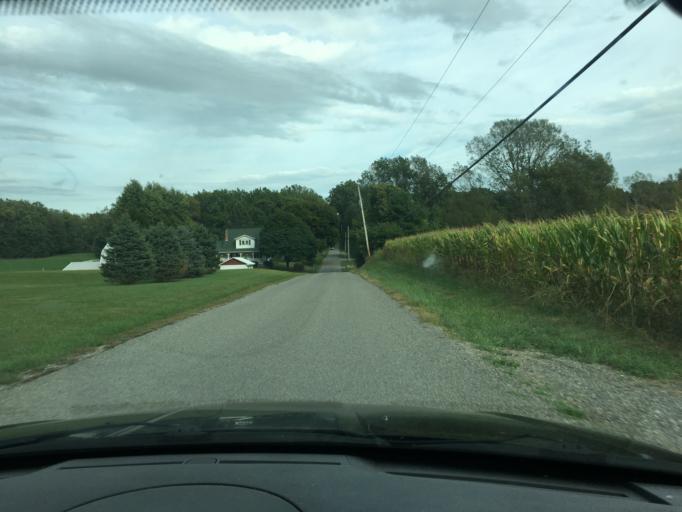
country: US
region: Ohio
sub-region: Logan County
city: Bellefontaine
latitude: 40.3186
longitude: -83.7811
